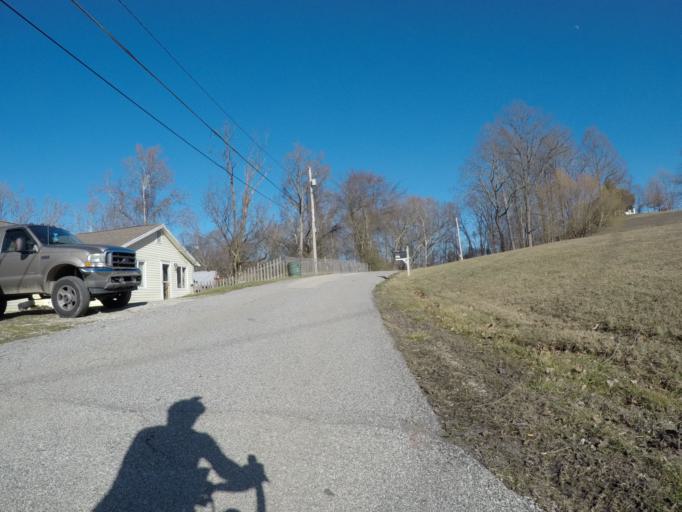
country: US
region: West Virginia
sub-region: Wayne County
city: Ceredo
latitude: 38.3832
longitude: -82.5653
